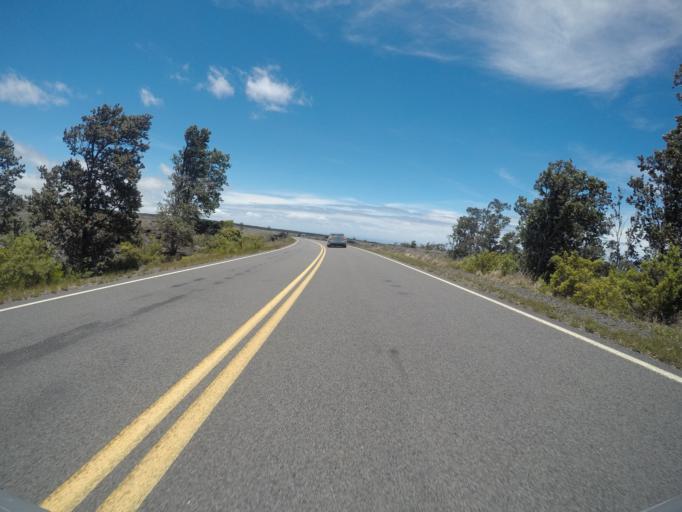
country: US
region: Hawaii
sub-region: Hawaii County
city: Volcano
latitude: 19.3375
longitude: -155.2067
